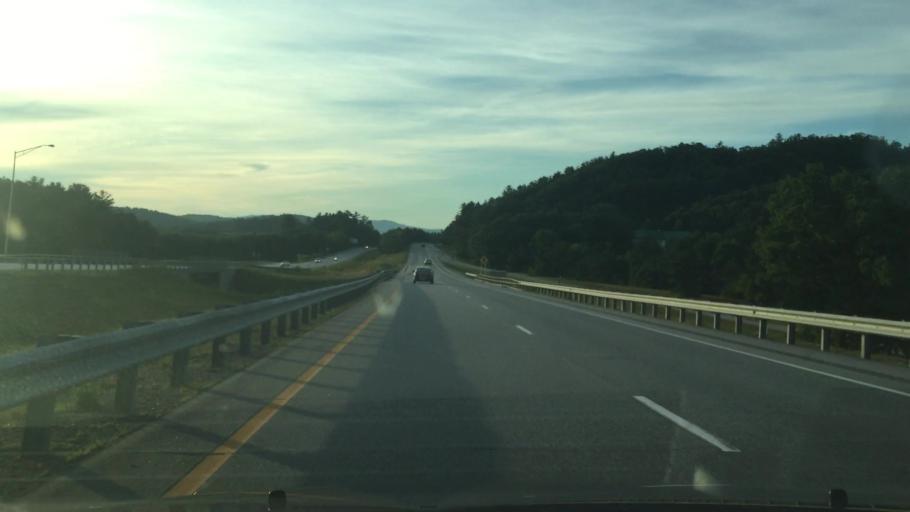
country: US
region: New Hampshire
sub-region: Grafton County
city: Ashland
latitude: 43.6968
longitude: -71.6448
